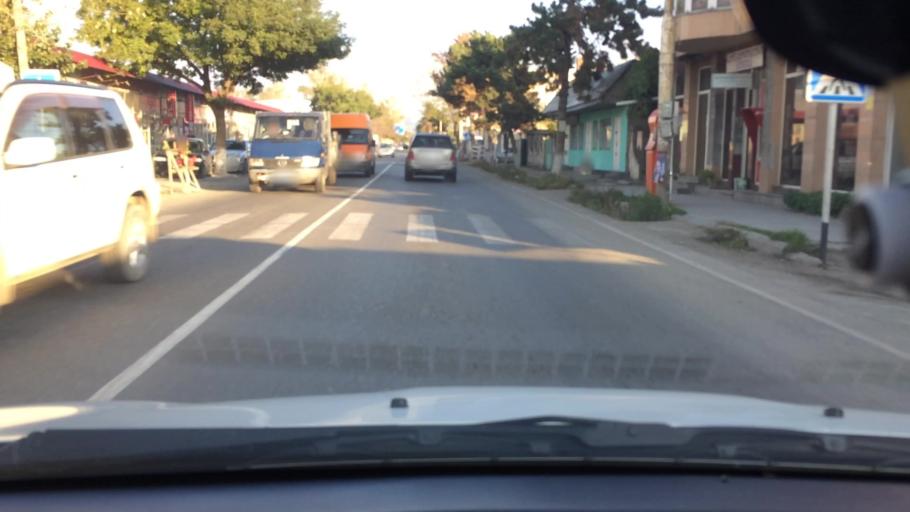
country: GE
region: Shida Kartli
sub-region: Khashuris Raioni
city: Khashuri
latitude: 41.9870
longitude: 43.5940
